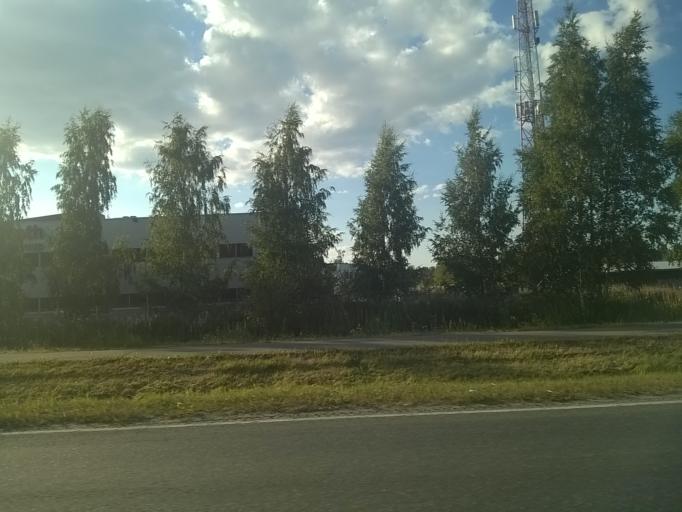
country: FI
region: Pirkanmaa
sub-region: Tampere
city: Tampere
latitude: 61.4638
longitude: 23.7567
